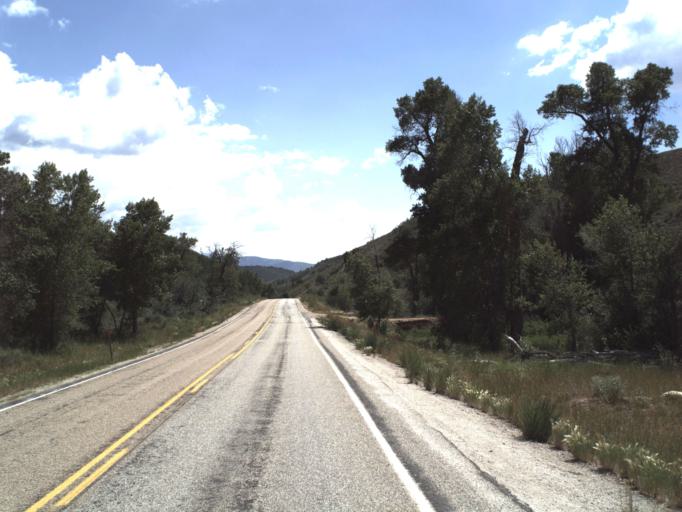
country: US
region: Utah
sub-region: Weber County
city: Wolf Creek
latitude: 41.3677
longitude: -111.5906
